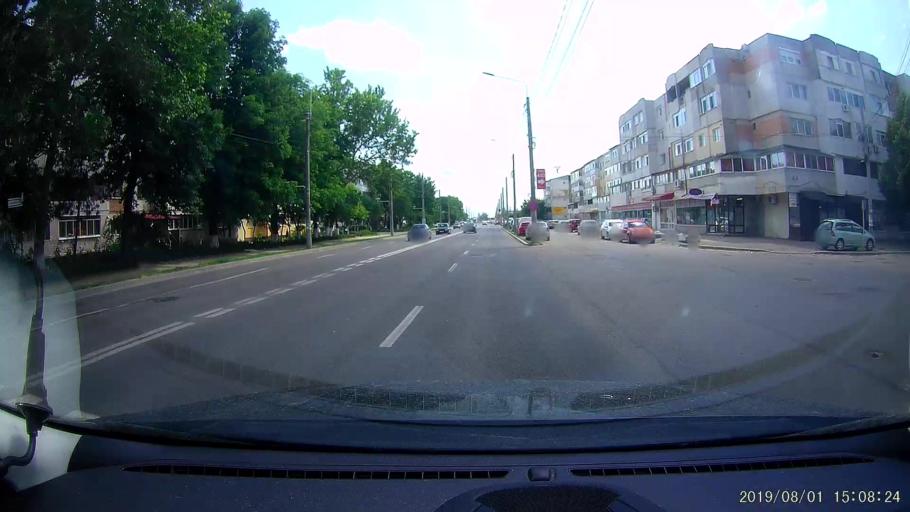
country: RO
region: Braila
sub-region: Municipiul Braila
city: Braila
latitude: 45.2420
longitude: 27.9458
